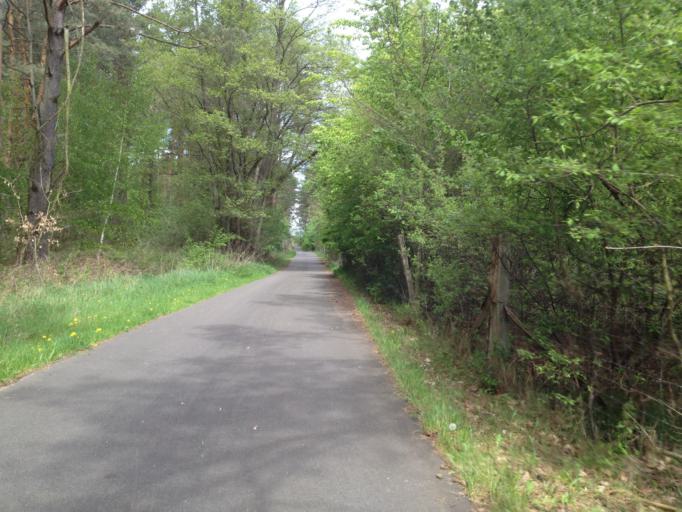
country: DE
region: Brandenburg
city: Lychen
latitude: 53.2772
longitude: 13.3059
